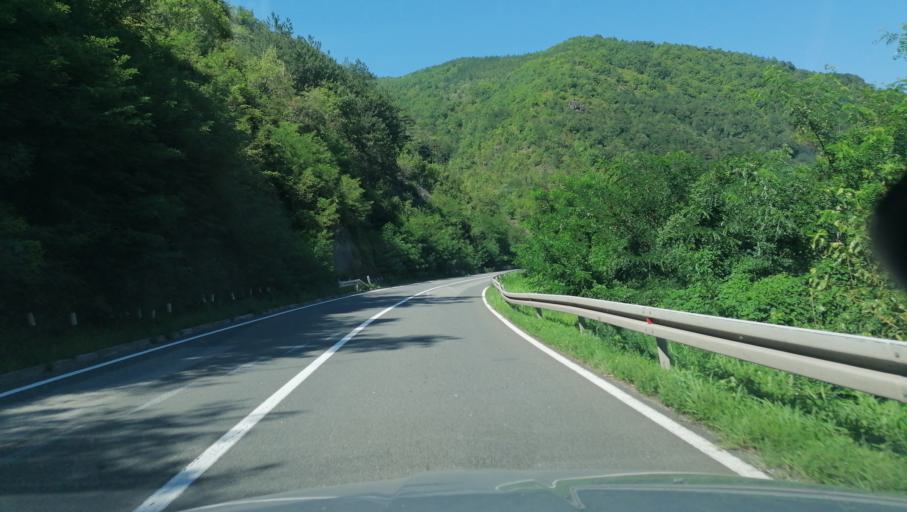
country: RS
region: Central Serbia
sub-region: Raski Okrug
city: Kraljevo
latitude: 43.6305
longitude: 20.5424
